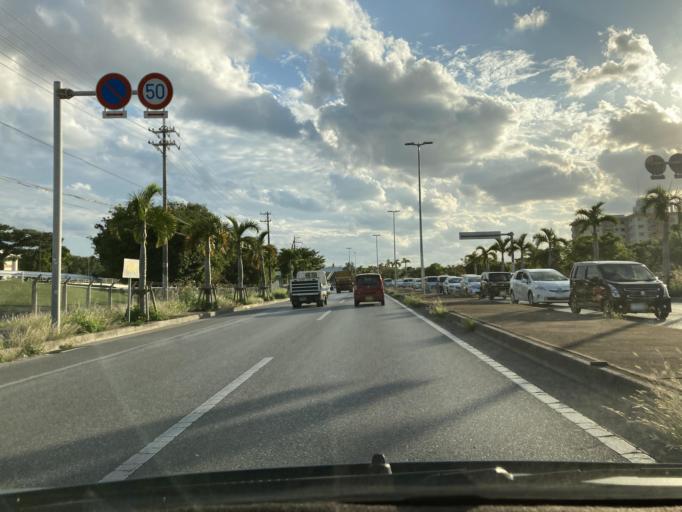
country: JP
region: Okinawa
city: Chatan
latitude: 26.3057
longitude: 127.7799
